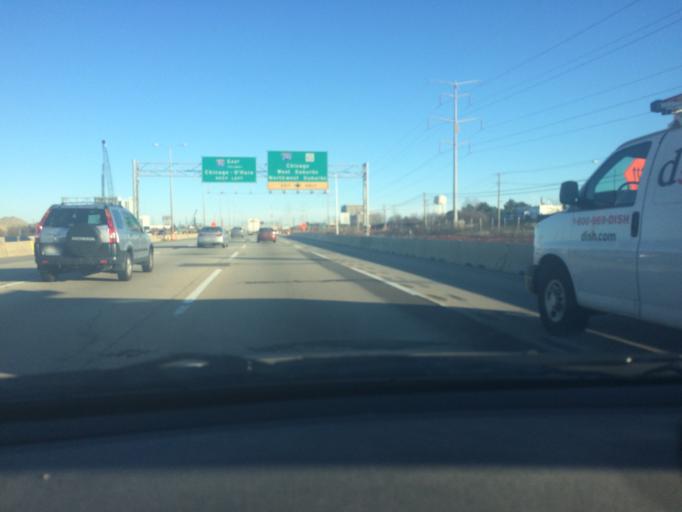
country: US
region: Illinois
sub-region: Cook County
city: Hoffman Estates
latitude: 42.0606
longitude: -88.0535
